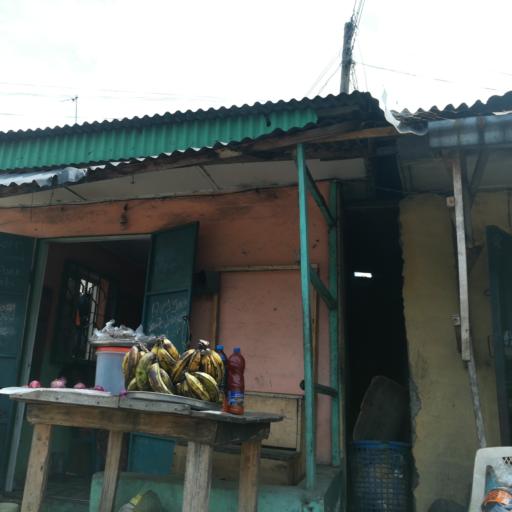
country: NG
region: Rivers
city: Port Harcourt
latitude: 4.7817
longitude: 7.0335
